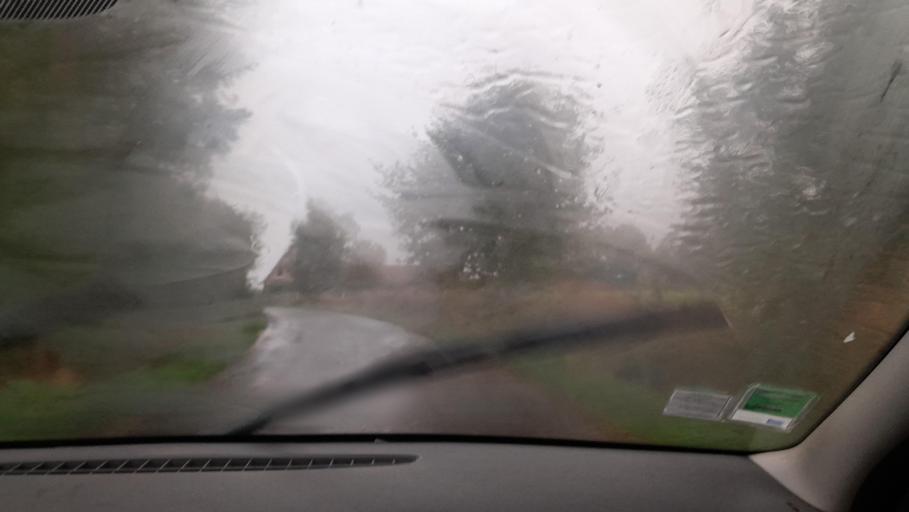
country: FR
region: Pays de la Loire
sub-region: Departement de la Mayenne
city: Ballots
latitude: 47.8589
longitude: -1.0669
